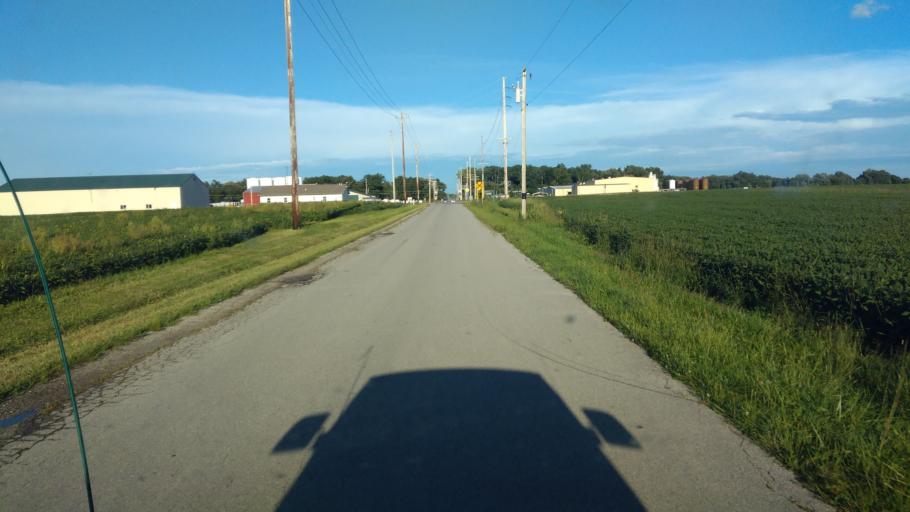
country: US
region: Ohio
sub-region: Wyandot County
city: Upper Sandusky
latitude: 40.8471
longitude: -83.3057
